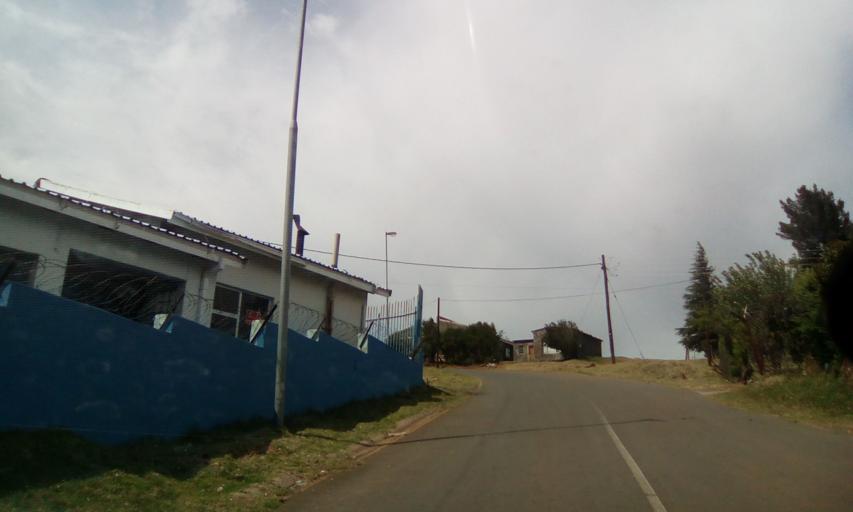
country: LS
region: Qacha's Nek
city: Qacha's Nek
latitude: -30.1141
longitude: 28.6772
